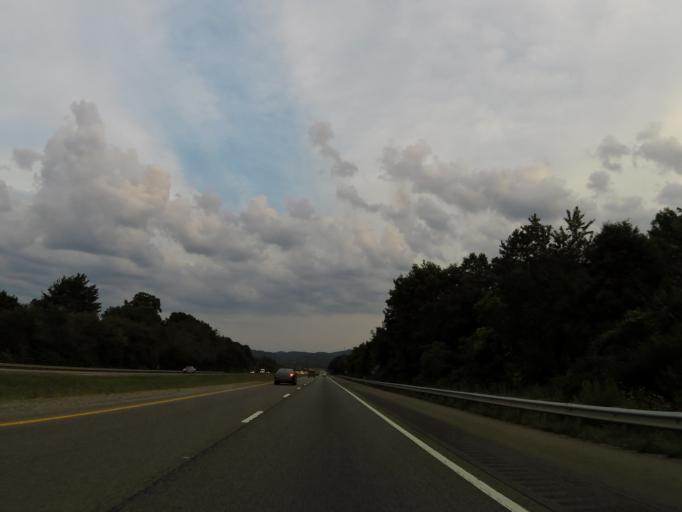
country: US
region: Tennessee
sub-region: Anderson County
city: Norris
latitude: 36.1781
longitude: -84.0913
